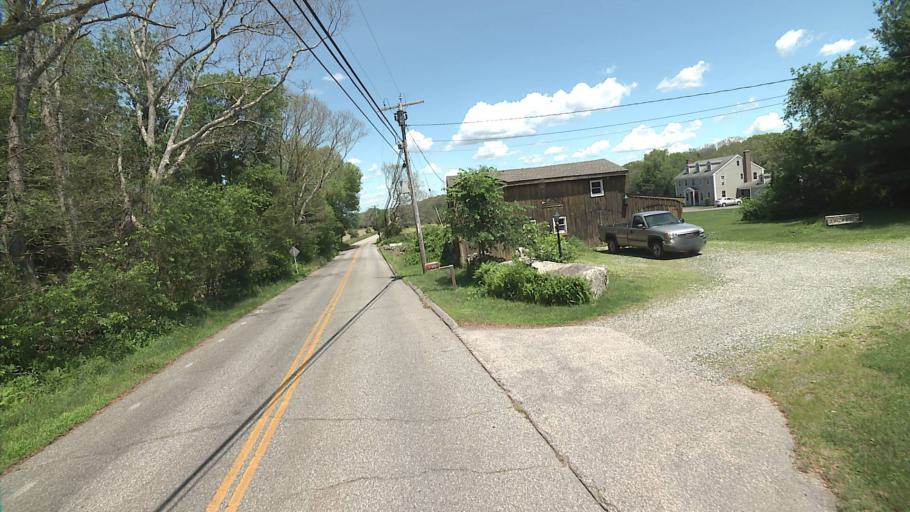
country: US
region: Connecticut
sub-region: New London County
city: Preston City
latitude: 41.5342
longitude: -71.8800
